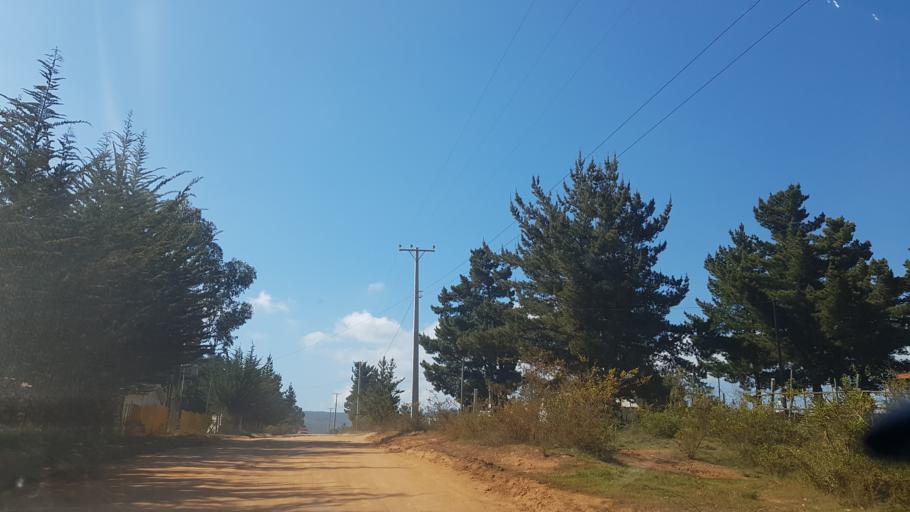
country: CL
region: Valparaiso
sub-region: Provincia de Valparaiso
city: Valparaiso
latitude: -33.1342
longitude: -71.6594
